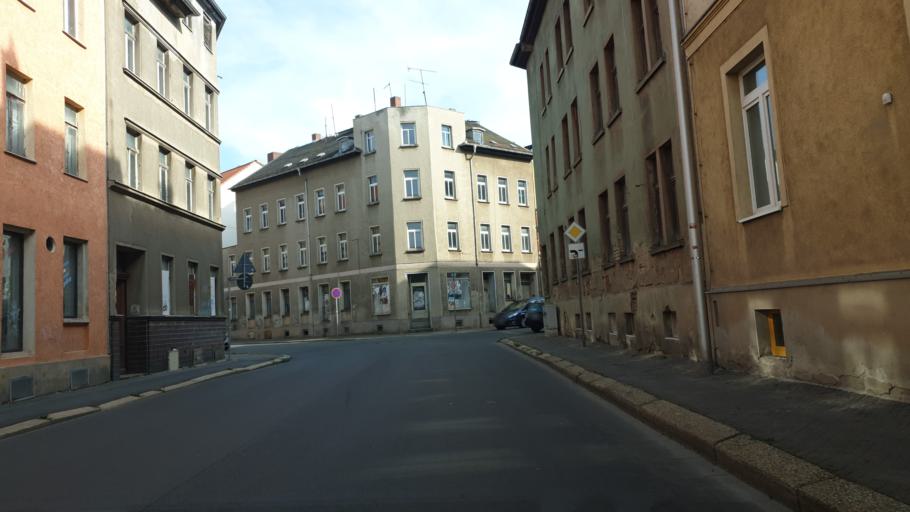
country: DE
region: Thuringia
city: Gera
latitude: 50.8528
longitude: 12.0844
